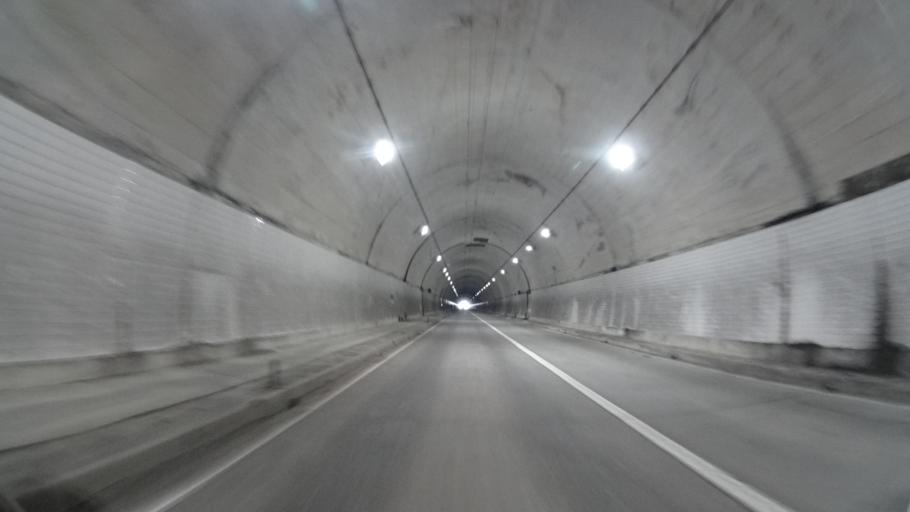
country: JP
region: Ehime
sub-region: Nishiuwa-gun
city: Ikata-cho
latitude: 33.3900
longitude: 132.1352
